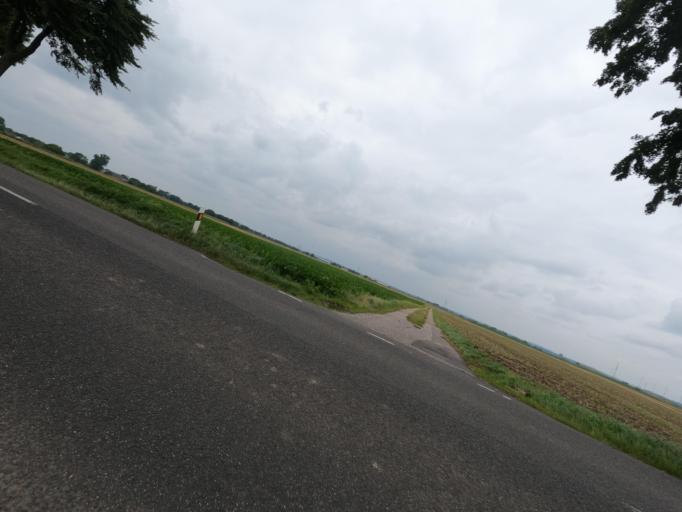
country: DE
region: North Rhine-Westphalia
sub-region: Regierungsbezirk Koln
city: Linnich
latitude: 50.9918
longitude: 6.2216
